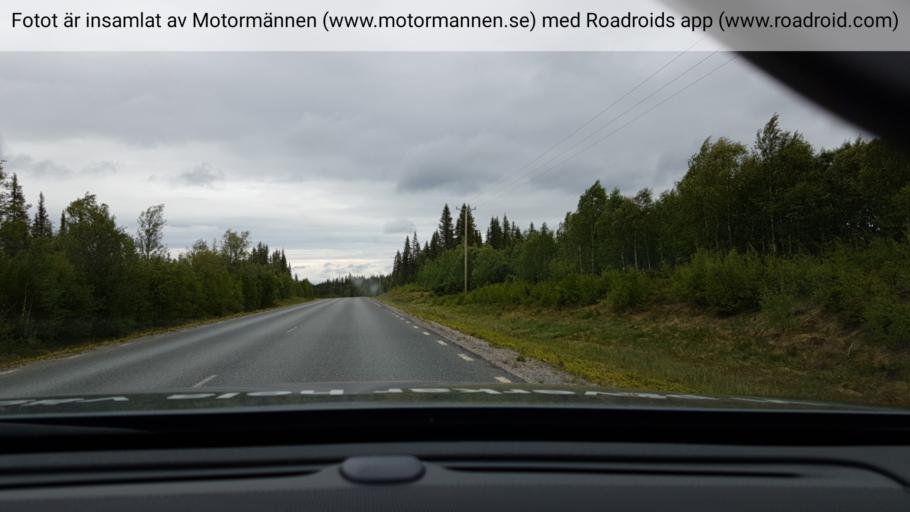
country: SE
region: Vaesterbotten
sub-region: Lycksele Kommun
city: Soderfors
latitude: 64.4396
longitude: 18.1137
